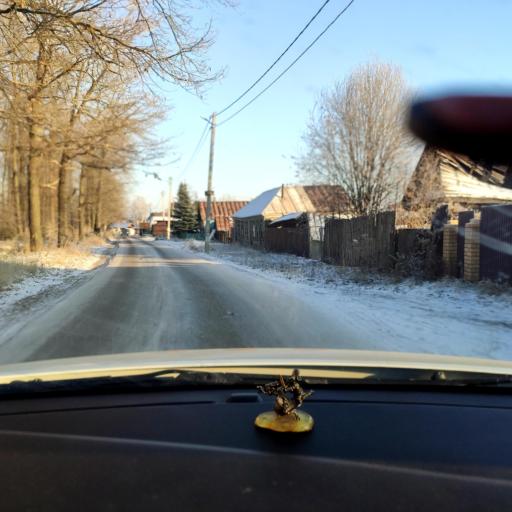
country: RU
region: Tatarstan
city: Stolbishchi
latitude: 55.6738
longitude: 49.1108
